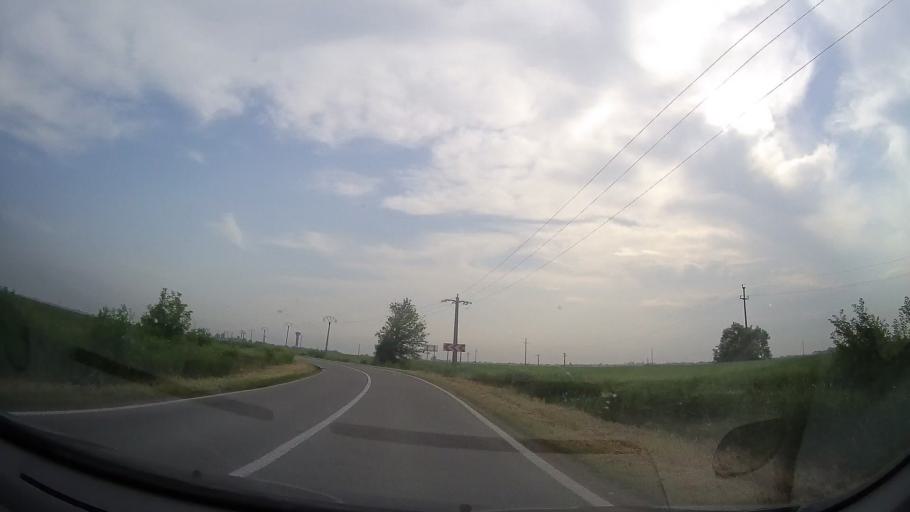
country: RO
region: Timis
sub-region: Comuna Parta
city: Parta
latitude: 45.6471
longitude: 21.1391
